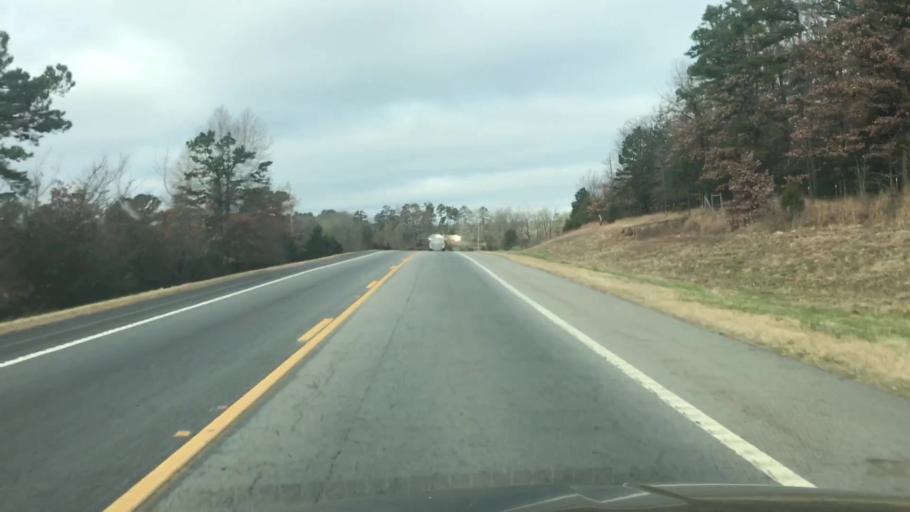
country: US
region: Arkansas
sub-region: Scott County
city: Waldron
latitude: 34.8390
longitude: -94.0505
